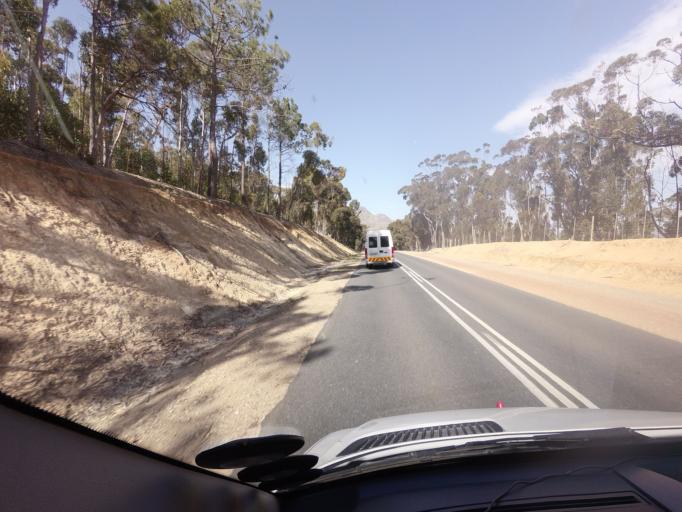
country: ZA
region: Western Cape
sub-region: Overberg District Municipality
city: Hermanus
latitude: -34.4048
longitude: 19.3651
